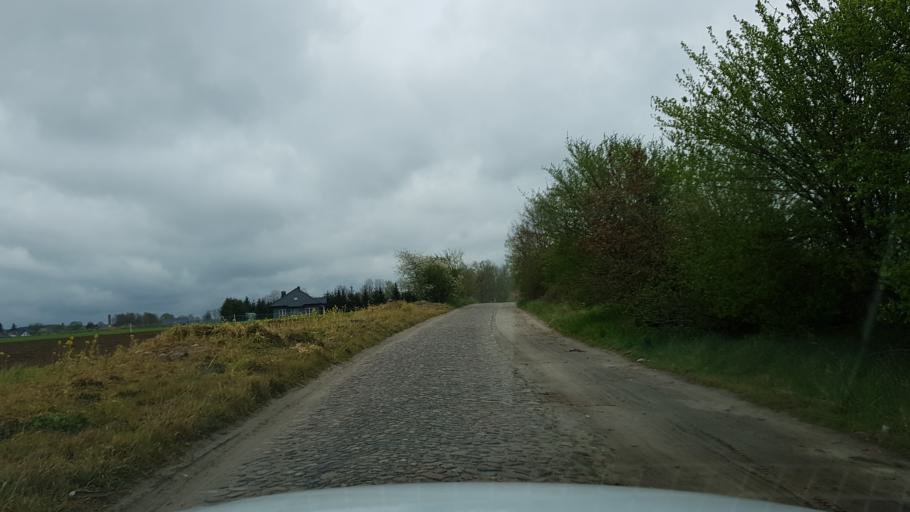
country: PL
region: West Pomeranian Voivodeship
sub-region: Powiat kolobrzeski
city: Ryman
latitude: 54.0325
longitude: 15.5235
